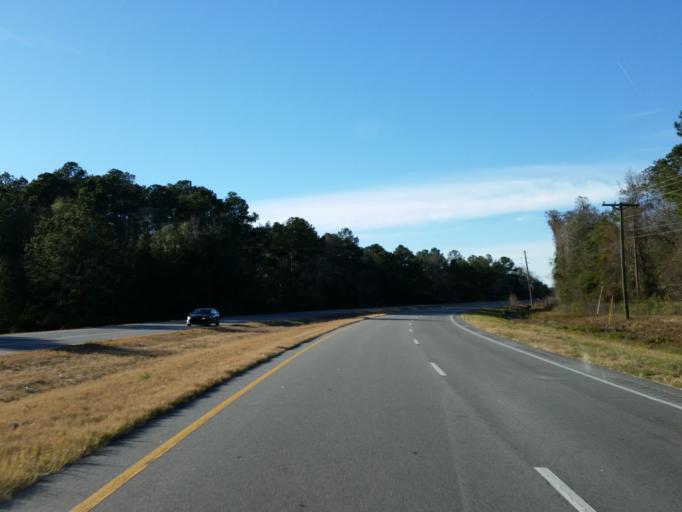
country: US
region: Georgia
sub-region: Lowndes County
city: Valdosta
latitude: 30.7657
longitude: -83.2257
